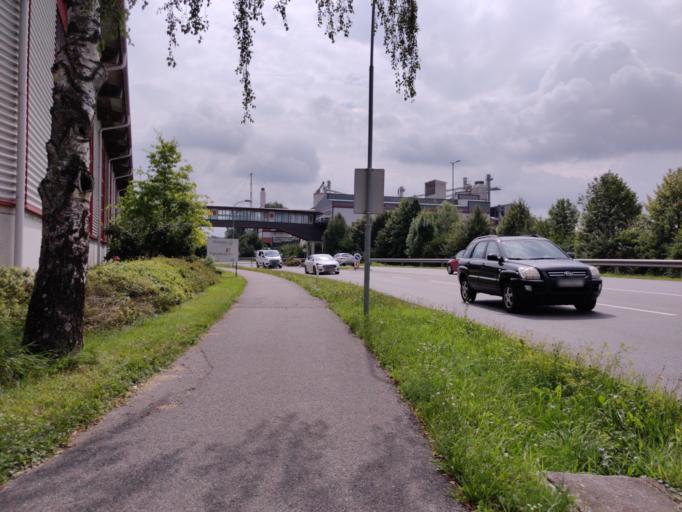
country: AT
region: Lower Austria
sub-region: Politischer Bezirk Melk
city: Ybbs an der Donau
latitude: 48.1671
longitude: 15.0881
